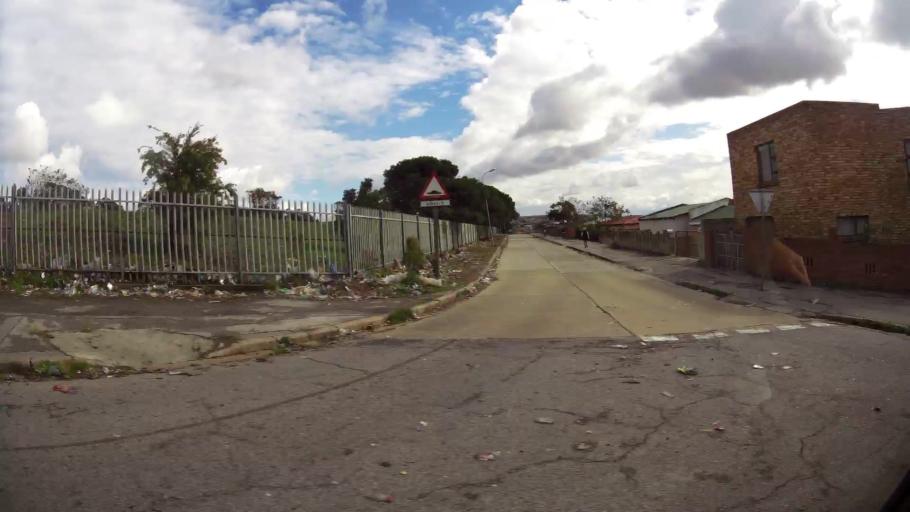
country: ZA
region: Eastern Cape
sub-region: Nelson Mandela Bay Metropolitan Municipality
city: Port Elizabeth
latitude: -33.9299
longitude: 25.5683
